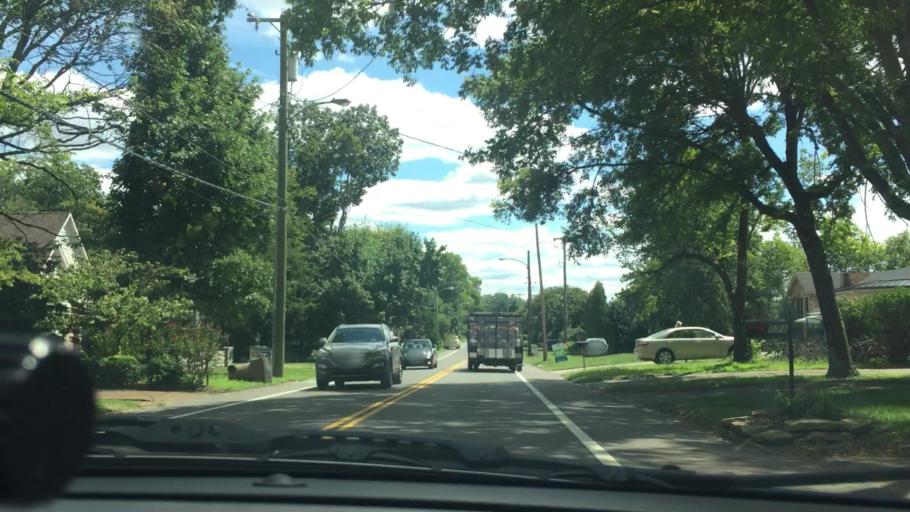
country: US
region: Tennessee
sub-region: Davidson County
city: Belle Meade
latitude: 36.1198
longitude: -86.8429
